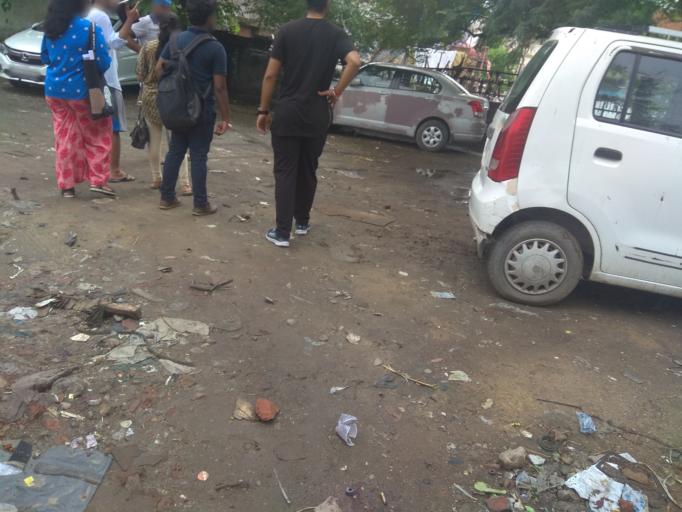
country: IN
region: NCT
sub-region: New Delhi
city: New Delhi
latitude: 28.5718
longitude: 77.2548
